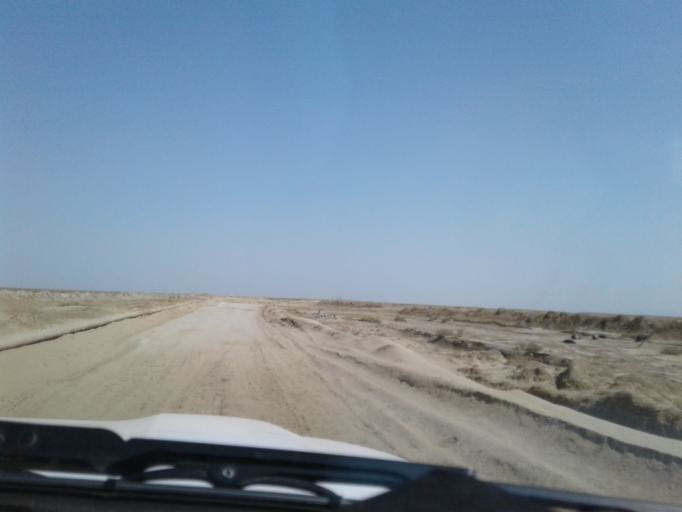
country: IR
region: Golestan
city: Gomishan
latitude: 37.8311
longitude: 53.9215
